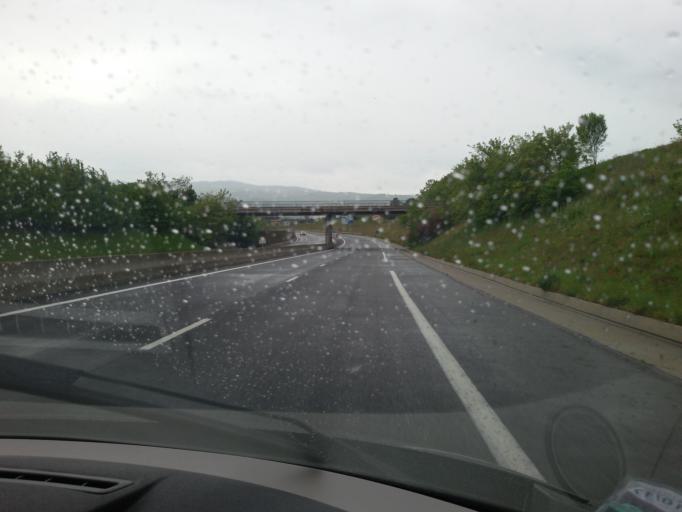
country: FR
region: Rhone-Alpes
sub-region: Departement de la Drome
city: Bourg-les-Valence
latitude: 44.9660
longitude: 4.8945
